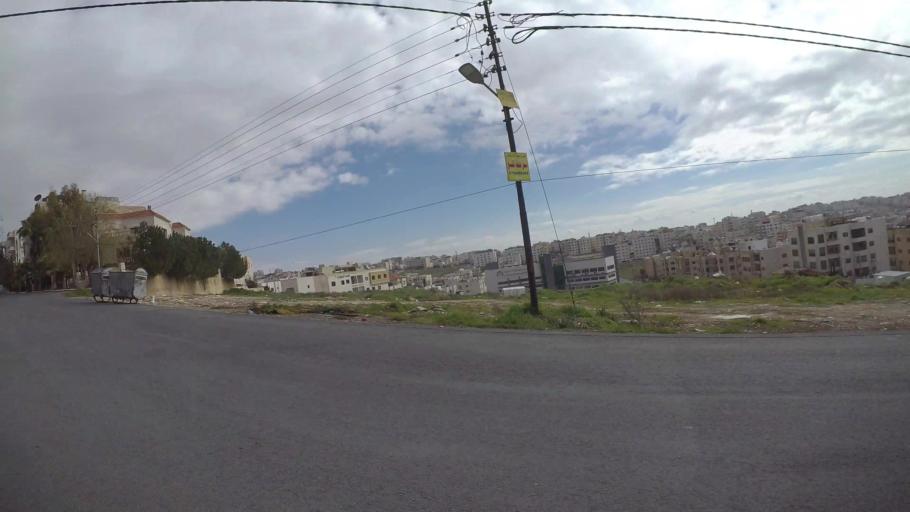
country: JO
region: Amman
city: Al Jubayhah
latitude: 32.0017
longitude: 35.8430
